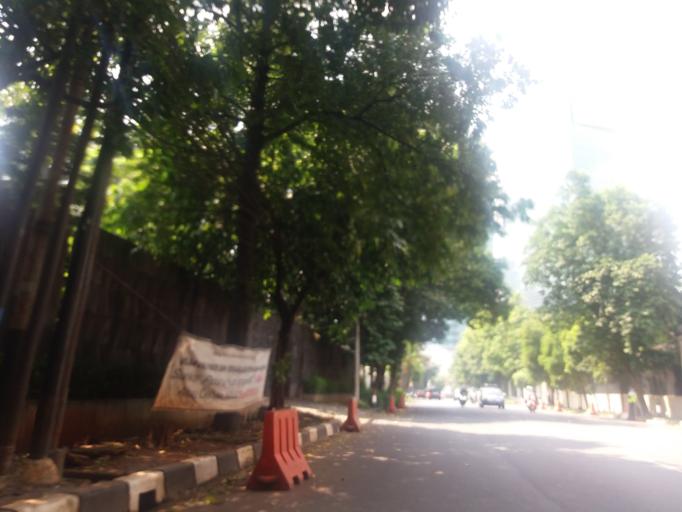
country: ID
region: Jakarta Raya
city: Jakarta
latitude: -6.2334
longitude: 106.8292
